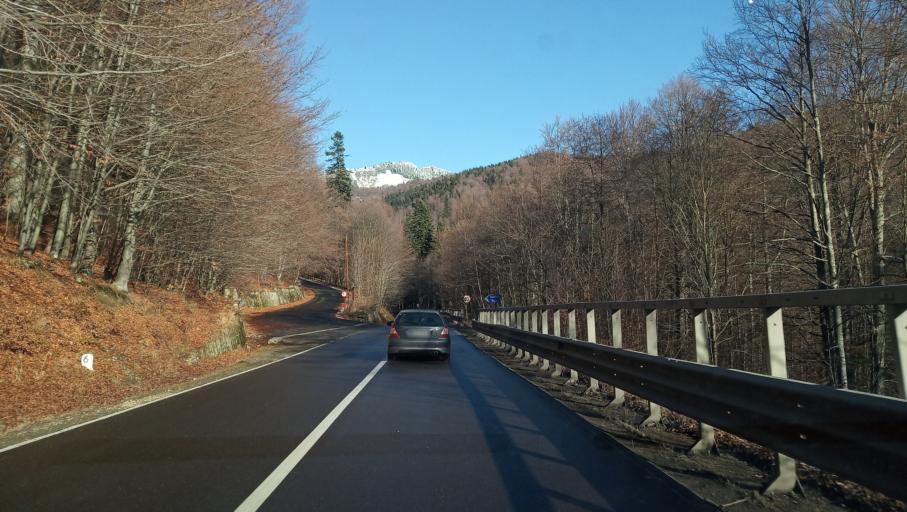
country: RO
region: Brasov
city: Crivina
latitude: 45.4691
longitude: 25.9313
